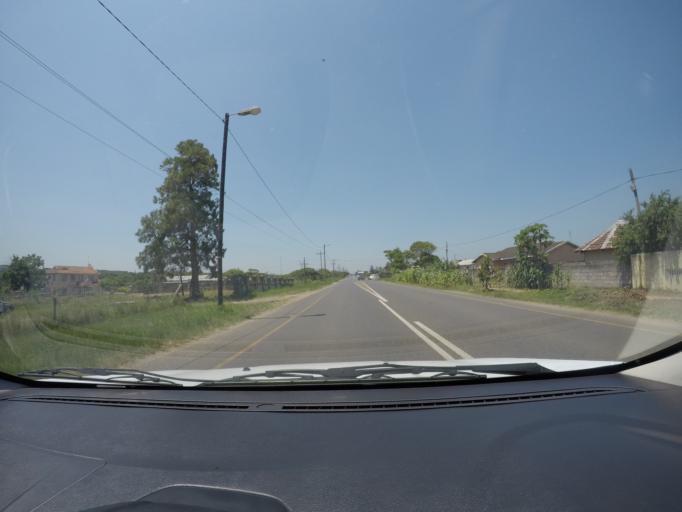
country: ZA
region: KwaZulu-Natal
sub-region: uThungulu District Municipality
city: eSikhawini
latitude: -28.8794
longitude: 31.8915
